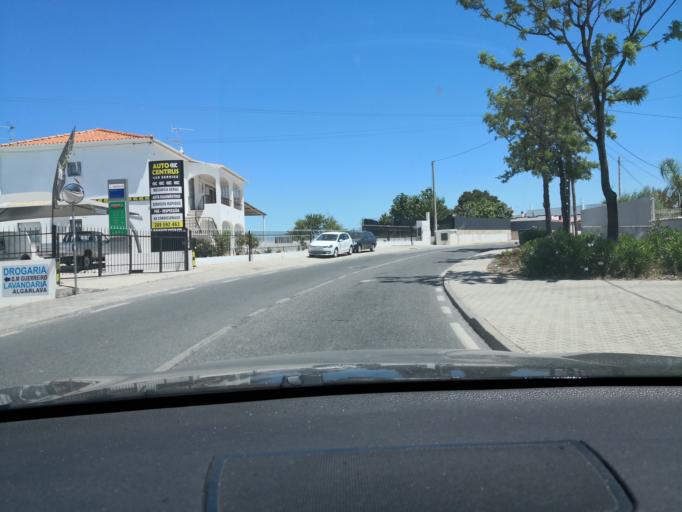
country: PT
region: Faro
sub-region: Albufeira
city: Ferreiras
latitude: 37.1069
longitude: -8.2135
